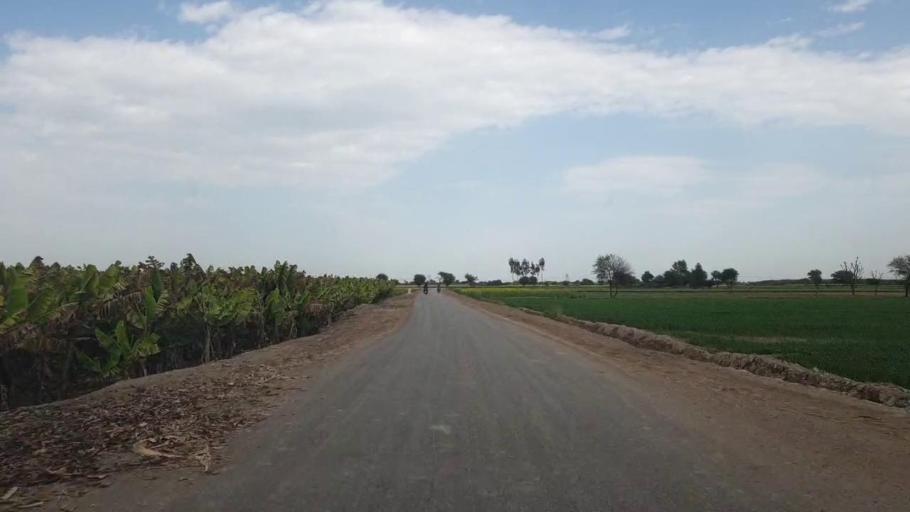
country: PK
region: Sindh
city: Hala
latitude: 25.9676
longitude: 68.3976
